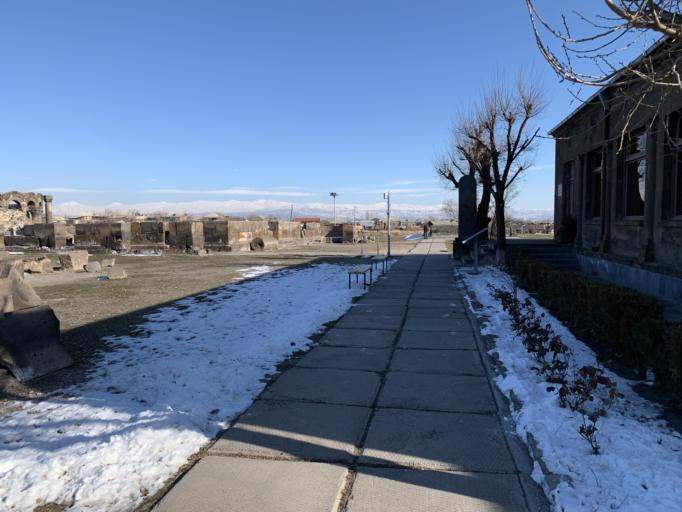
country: AM
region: Armavir
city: Voskehat
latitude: 40.1598
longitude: 44.3358
